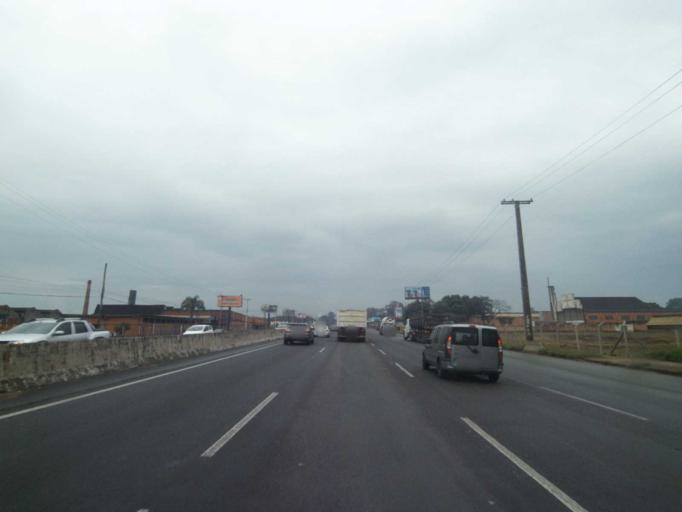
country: BR
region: Rio Grande do Sul
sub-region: Sapucaia Do Sul
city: Sapucaia
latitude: -29.8242
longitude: -51.1718
